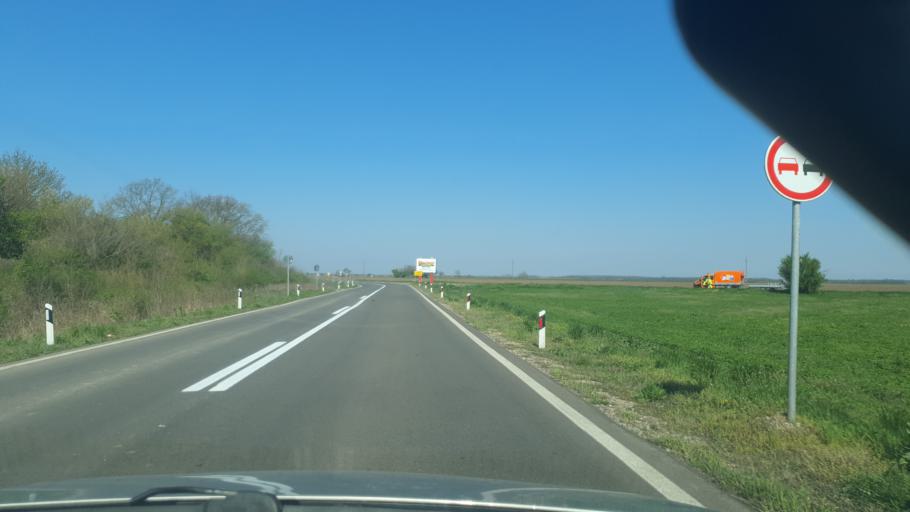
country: RS
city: Kolut
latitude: 45.8397
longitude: 18.9935
